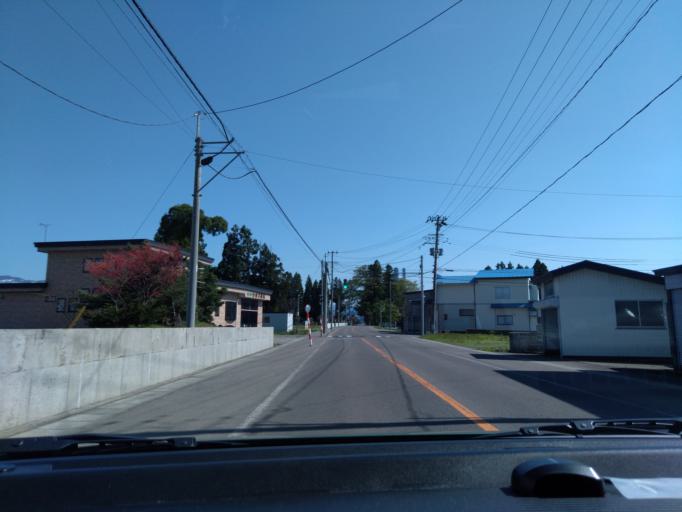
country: JP
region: Akita
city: Kakunodatemachi
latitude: 39.5303
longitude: 140.5858
